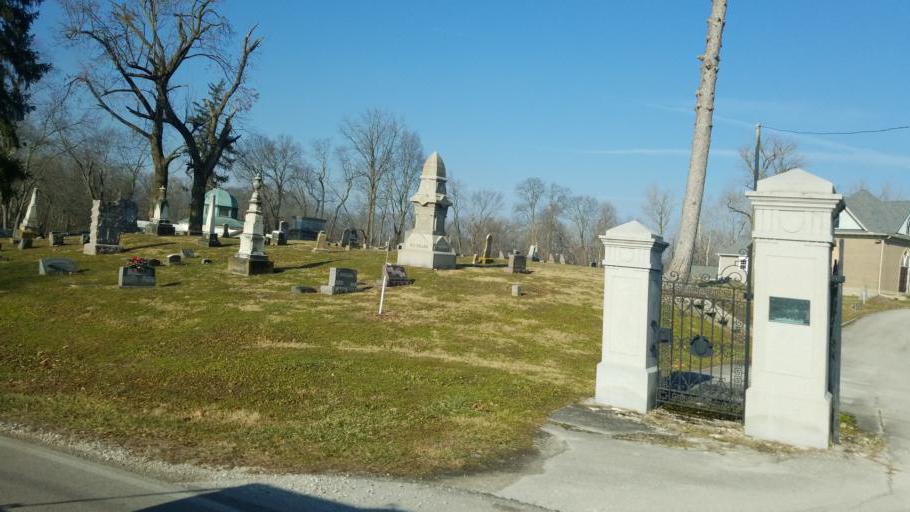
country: US
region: Ohio
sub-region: Seneca County
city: Tiffin
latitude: 41.1003
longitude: -83.1525
